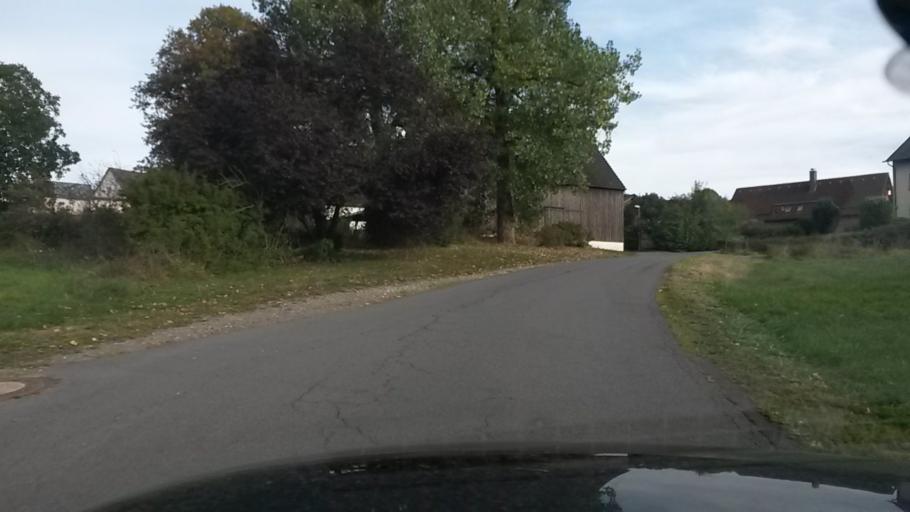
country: DE
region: North Rhine-Westphalia
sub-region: Regierungsbezirk Arnsberg
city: Herscheid
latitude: 51.2137
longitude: 7.7562
